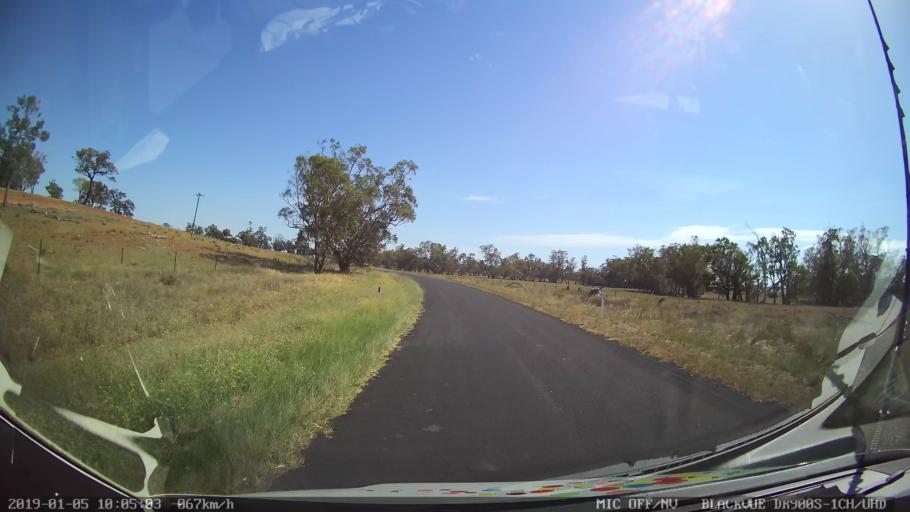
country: AU
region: New South Wales
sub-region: Gilgandra
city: Gilgandra
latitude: -31.6698
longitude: 148.8636
